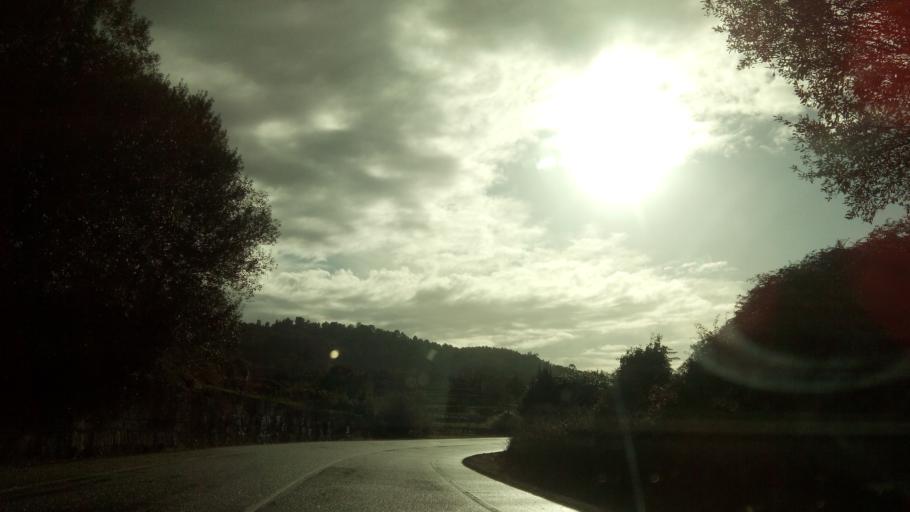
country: ES
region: Galicia
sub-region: Provincia de Pontevedra
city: Ponteareas
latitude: 42.2164
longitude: -8.4990
